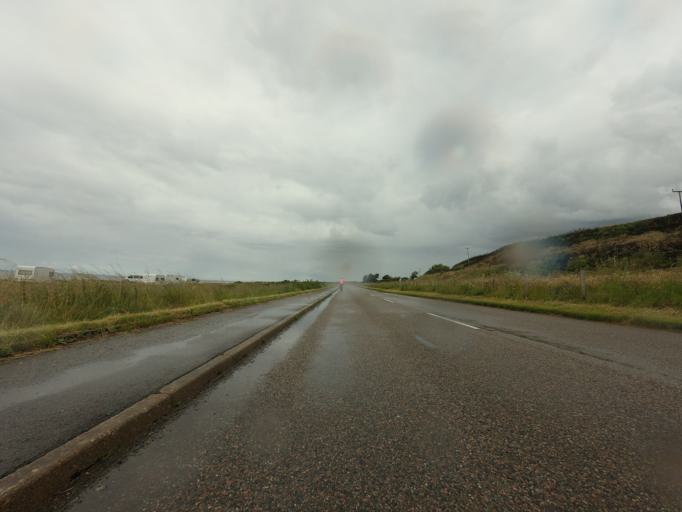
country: GB
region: Scotland
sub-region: Moray
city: Buckie
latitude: 57.6699
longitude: -2.9966
